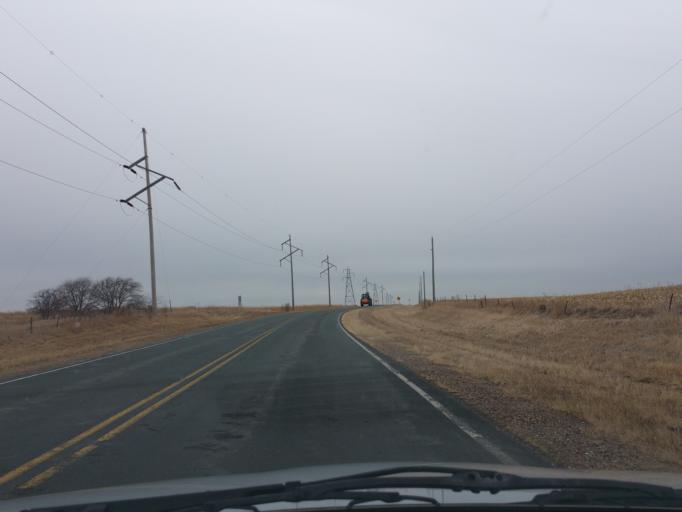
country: US
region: Wisconsin
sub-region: Saint Croix County
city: Roberts
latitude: 45.0358
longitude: -92.6007
